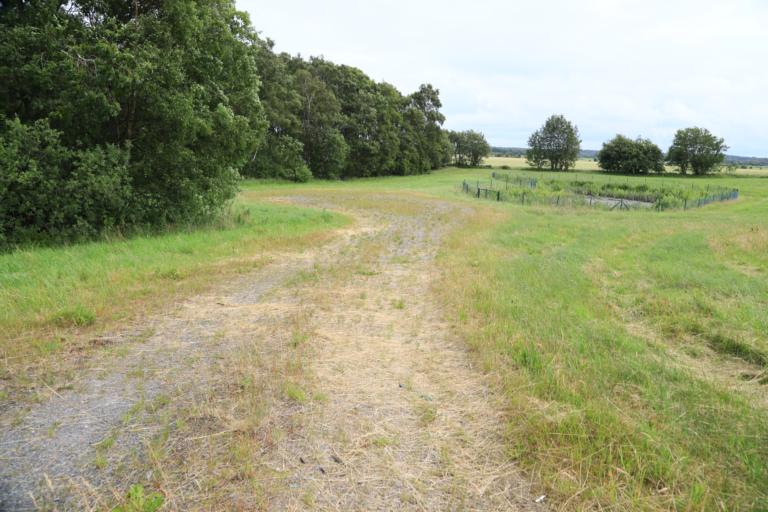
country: SE
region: Halland
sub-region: Varbergs Kommun
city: Traslovslage
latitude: 57.1008
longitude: 12.2983
